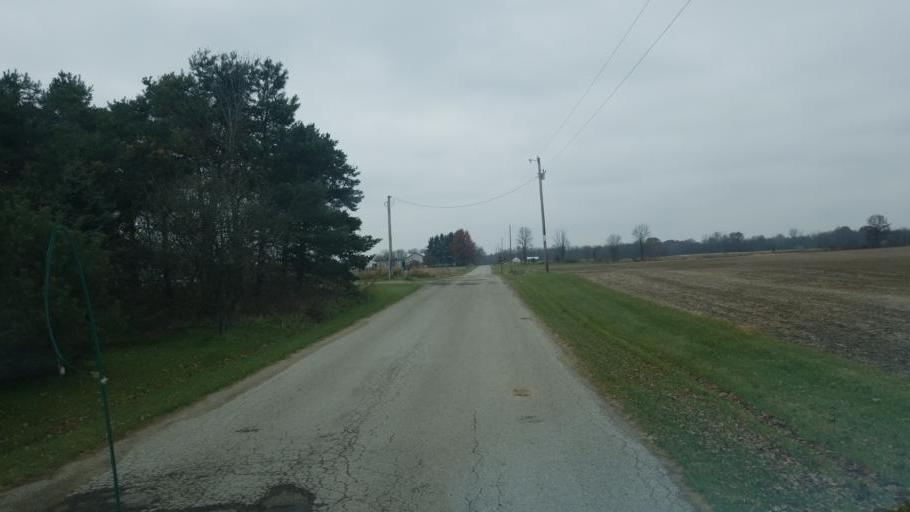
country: US
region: Ohio
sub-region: Morrow County
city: Cardington
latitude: 40.4253
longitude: -82.8346
